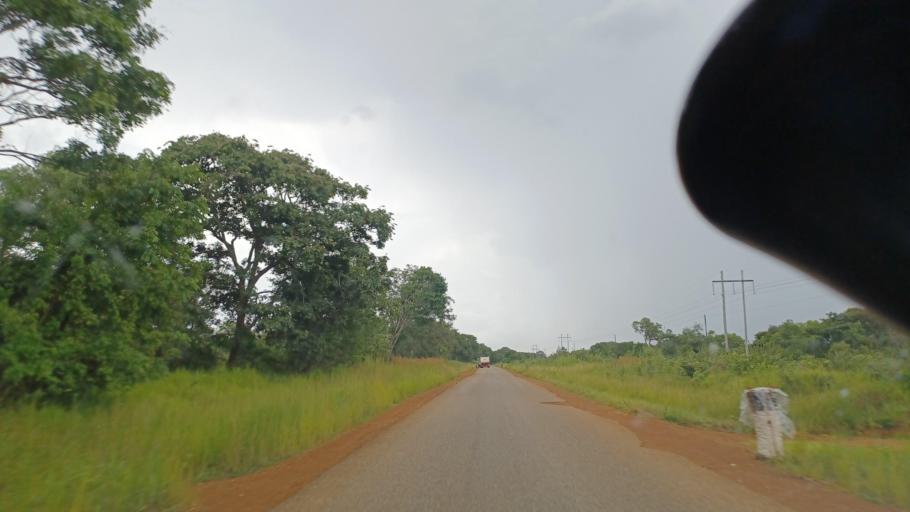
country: ZM
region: North-Western
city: Kasempa
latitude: -13.0426
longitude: 25.9927
